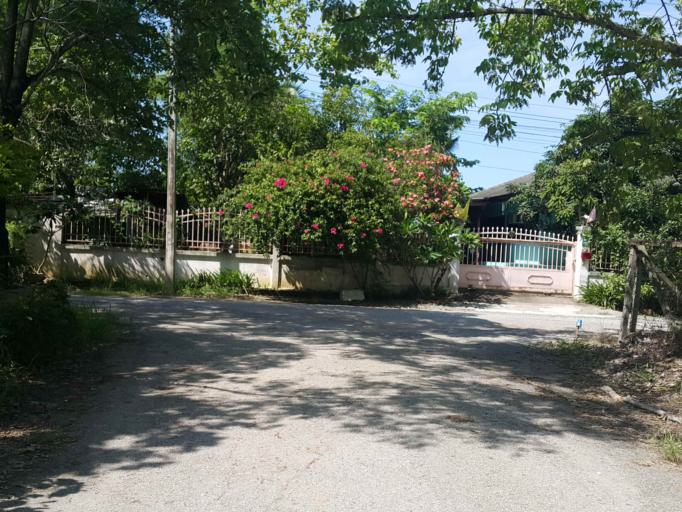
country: TH
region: Chiang Mai
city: San Kamphaeng
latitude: 18.7683
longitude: 99.0693
